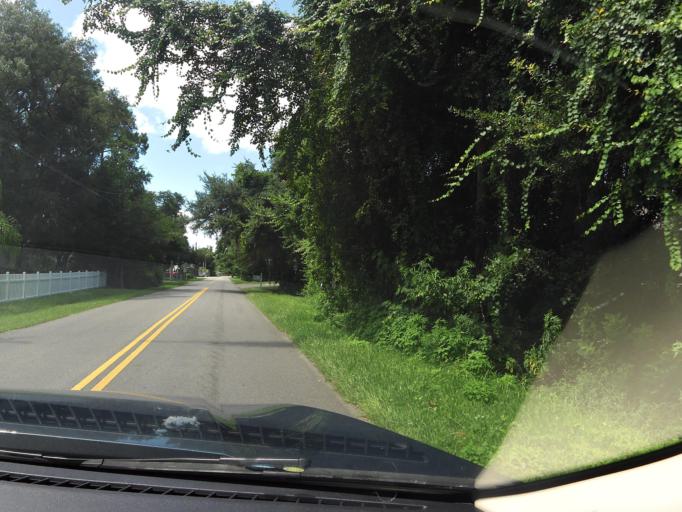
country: US
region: Florida
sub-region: Nassau County
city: Fernandina Beach
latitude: 30.6353
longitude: -81.4621
